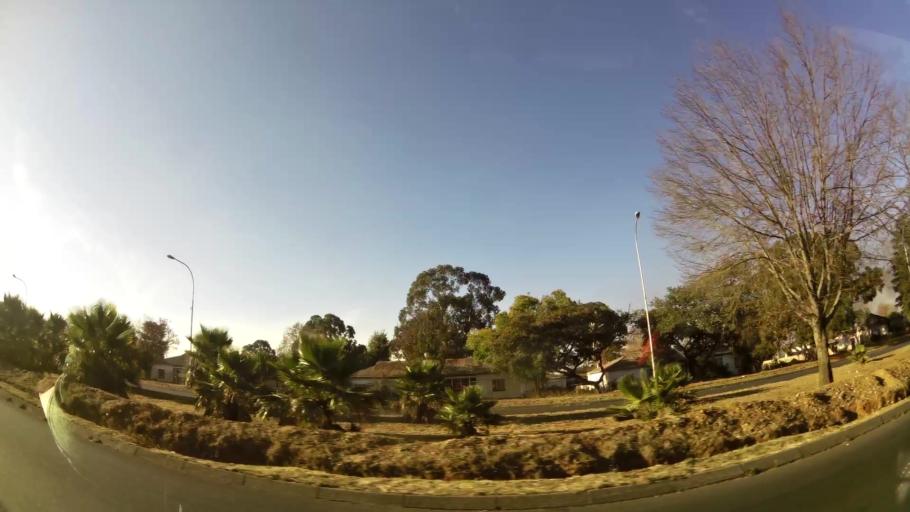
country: ZA
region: Gauteng
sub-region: City of Johannesburg Metropolitan Municipality
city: Roodepoort
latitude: -26.1730
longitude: 27.8752
